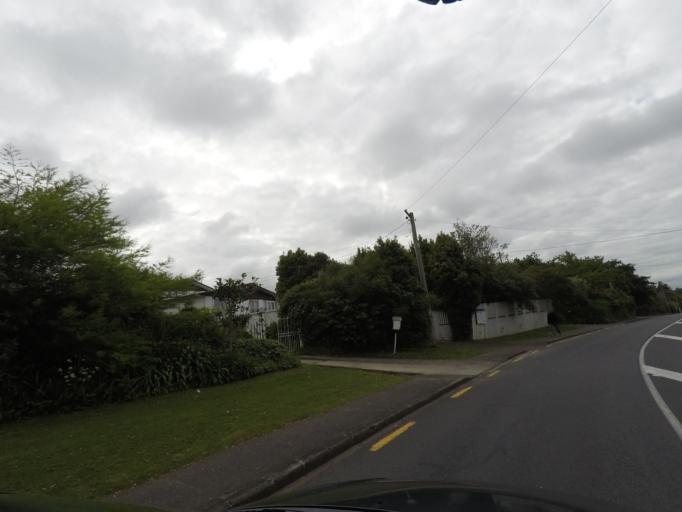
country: NZ
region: Auckland
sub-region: Auckland
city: Rosebank
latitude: -36.8431
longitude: 174.6064
